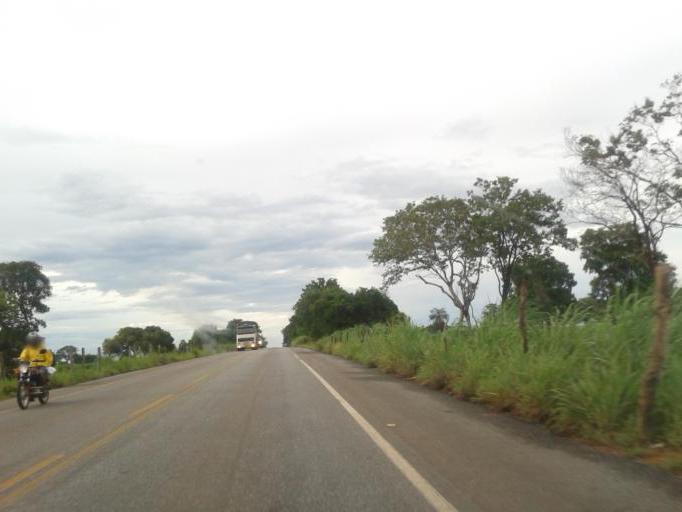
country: BR
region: Goias
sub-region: Mozarlandia
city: Mozarlandia
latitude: -14.7872
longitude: -50.5360
